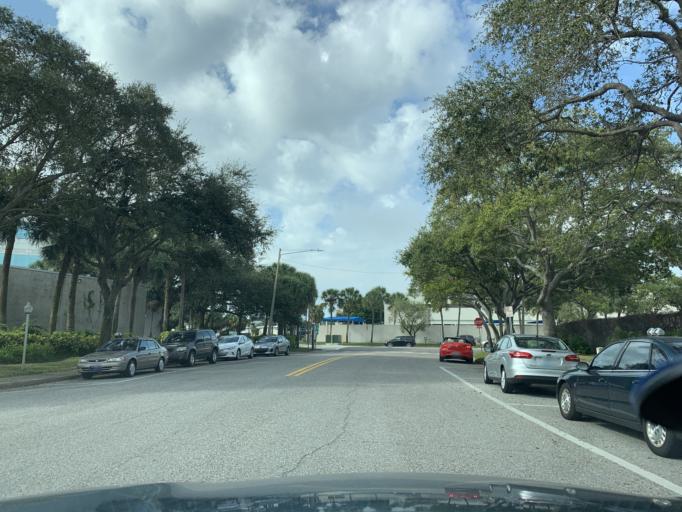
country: US
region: Florida
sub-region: Pinellas County
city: Saint Petersburg
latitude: 27.7623
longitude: -82.6333
